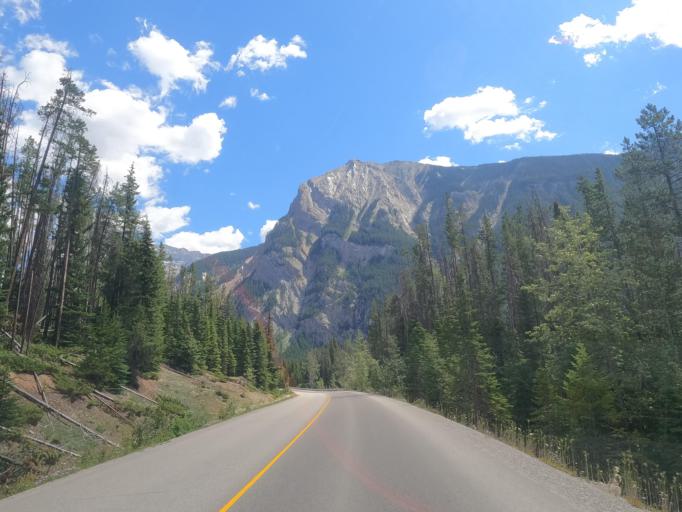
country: CA
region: Alberta
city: Lake Louise
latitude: 51.3800
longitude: -116.5179
